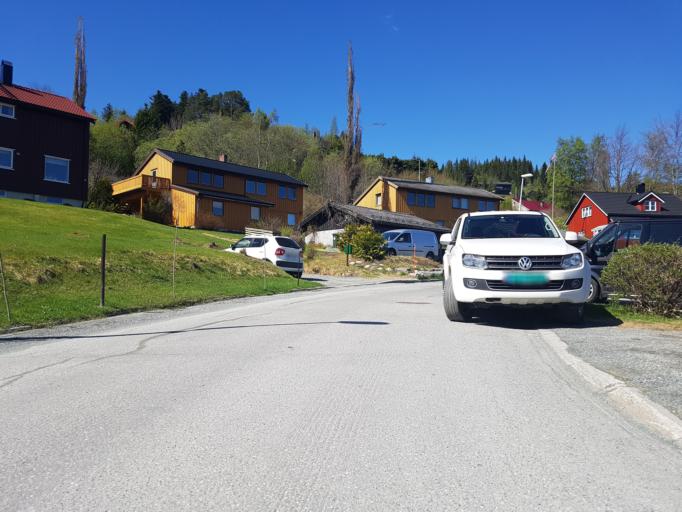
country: NO
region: Sor-Trondelag
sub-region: Trondheim
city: Trondheim
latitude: 63.4245
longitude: 10.3466
